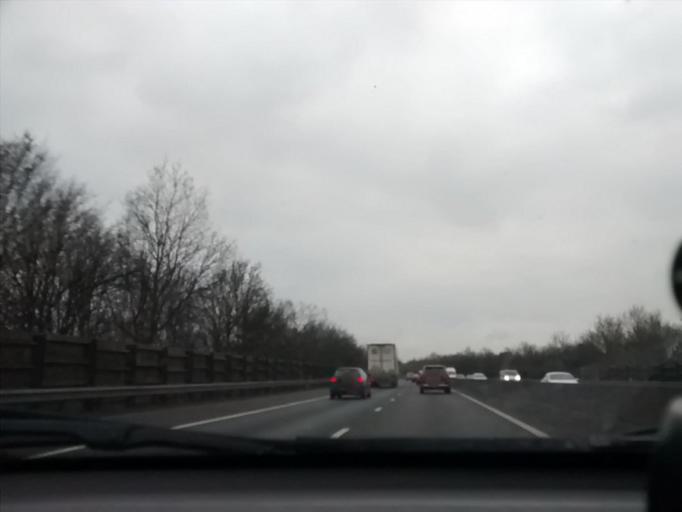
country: GB
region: England
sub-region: Essex
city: Elsenham
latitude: 51.9239
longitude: 0.2211
